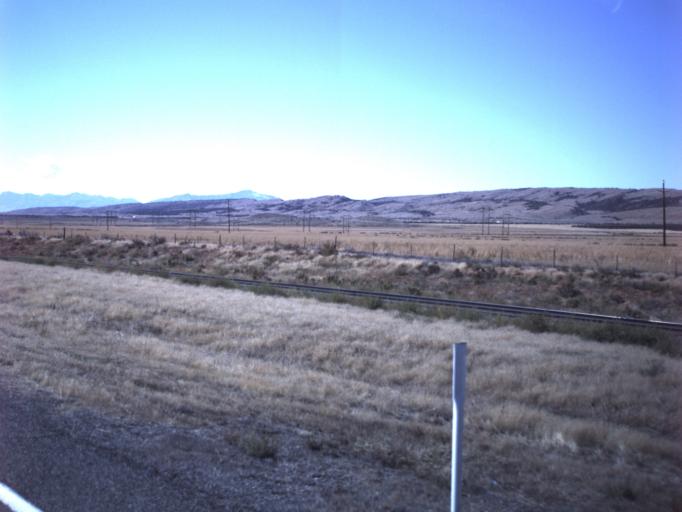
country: US
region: Utah
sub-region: Juab County
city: Nephi
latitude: 39.5544
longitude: -111.9217
